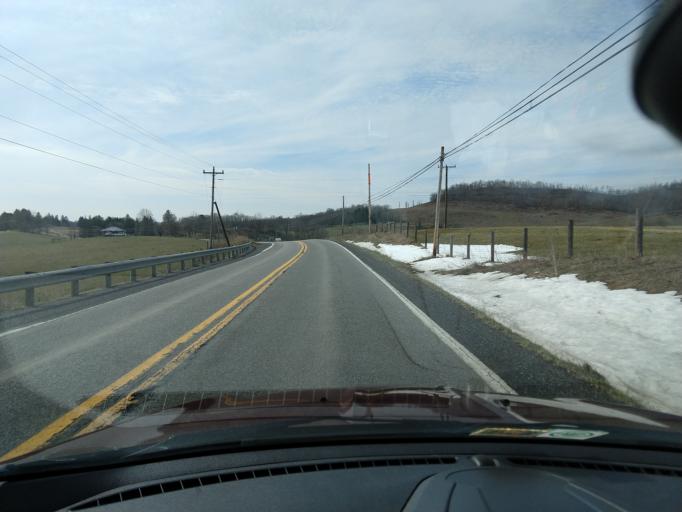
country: US
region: West Virginia
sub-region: Greenbrier County
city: Lewisburg
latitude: 37.8880
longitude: -80.4135
